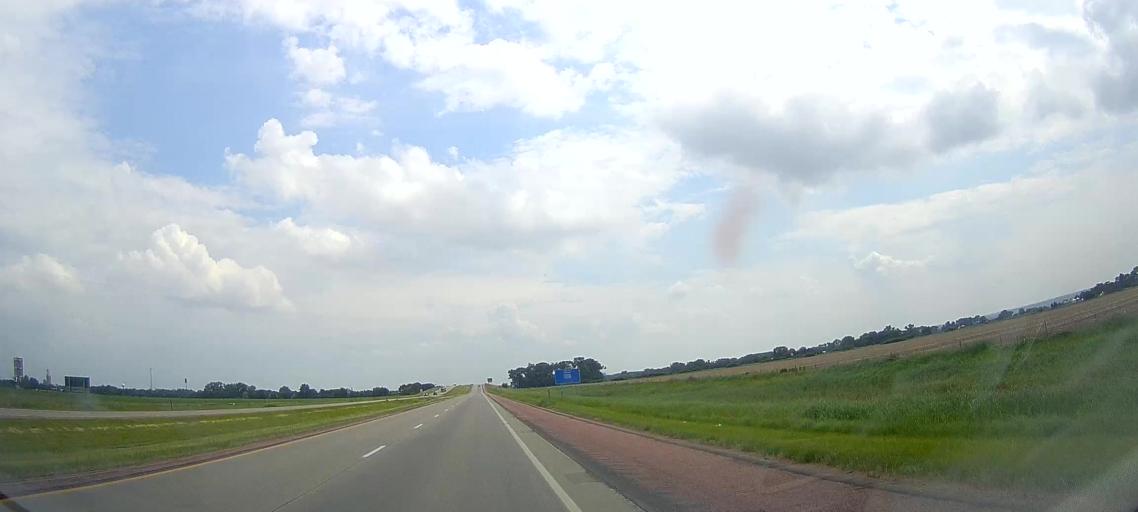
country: US
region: South Dakota
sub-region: Union County
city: Elk Point
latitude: 42.7015
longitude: -96.6974
